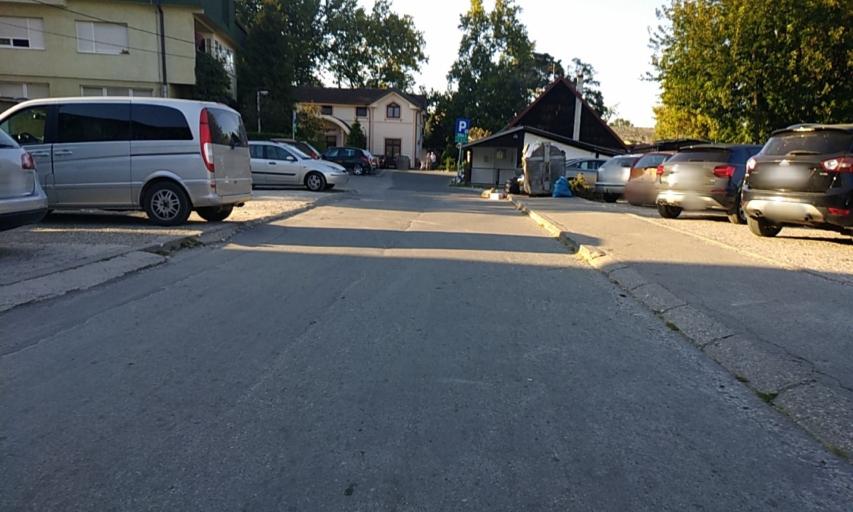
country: BA
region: Republika Srpska
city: Mejdan - Obilicevo
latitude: 44.7645
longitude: 17.1905
